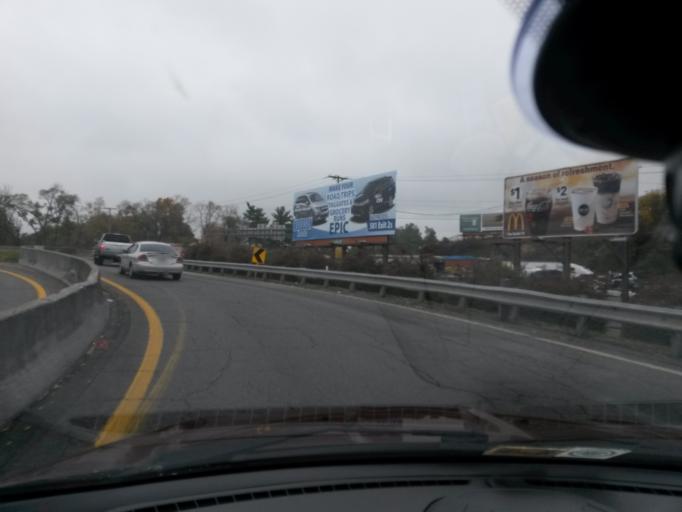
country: US
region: Virginia
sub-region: City of Roanoke
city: Roanoke
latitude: 37.2835
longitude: -79.9377
